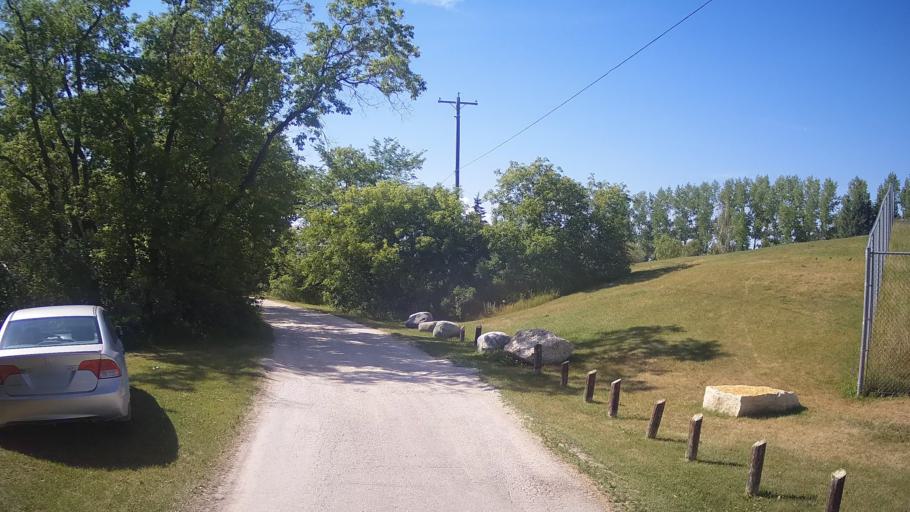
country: CA
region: Manitoba
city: Stonewall
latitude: 50.1416
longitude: -97.3269
